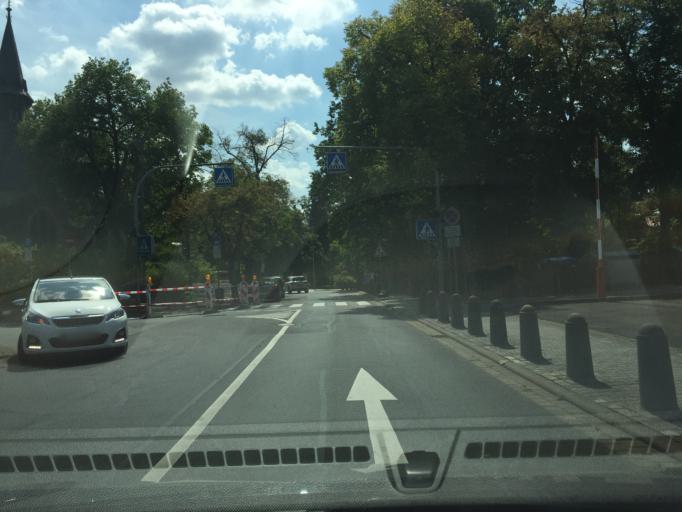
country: DE
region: Hesse
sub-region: Regierungsbezirk Giessen
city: Limburg an der Lahn
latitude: 50.3859
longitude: 8.0497
